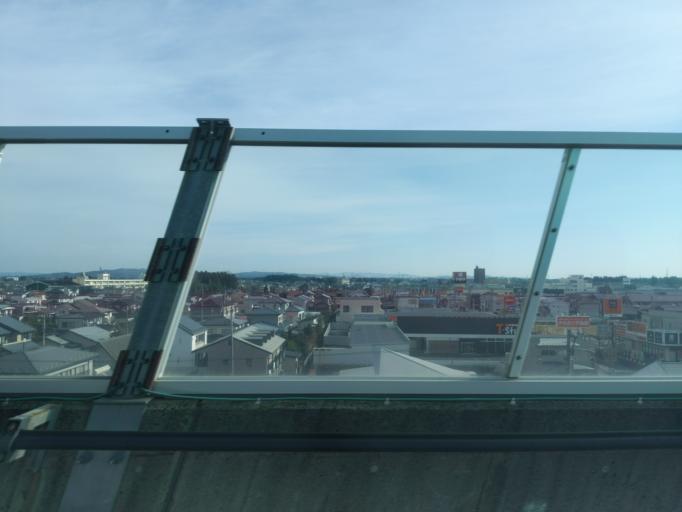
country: JP
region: Miyagi
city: Furukawa
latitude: 38.5760
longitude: 140.9693
